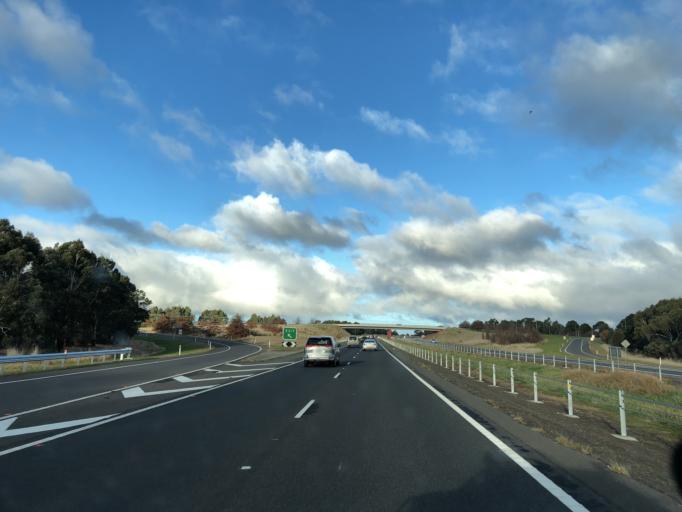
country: AU
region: Victoria
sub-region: Mount Alexander
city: Castlemaine
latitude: -37.2406
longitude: 144.4607
